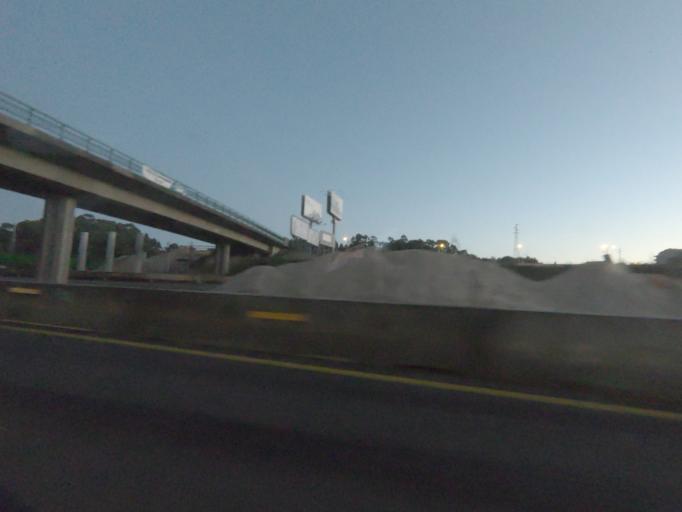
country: PT
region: Porto
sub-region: Maia
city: Pedroucos
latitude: 41.1990
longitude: -8.5712
